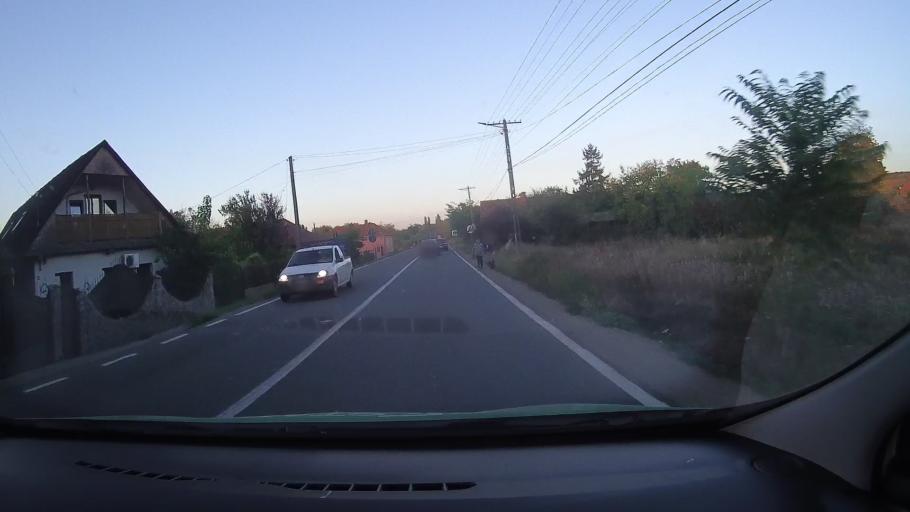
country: RO
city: Szekelyhid
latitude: 47.3381
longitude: 22.0911
